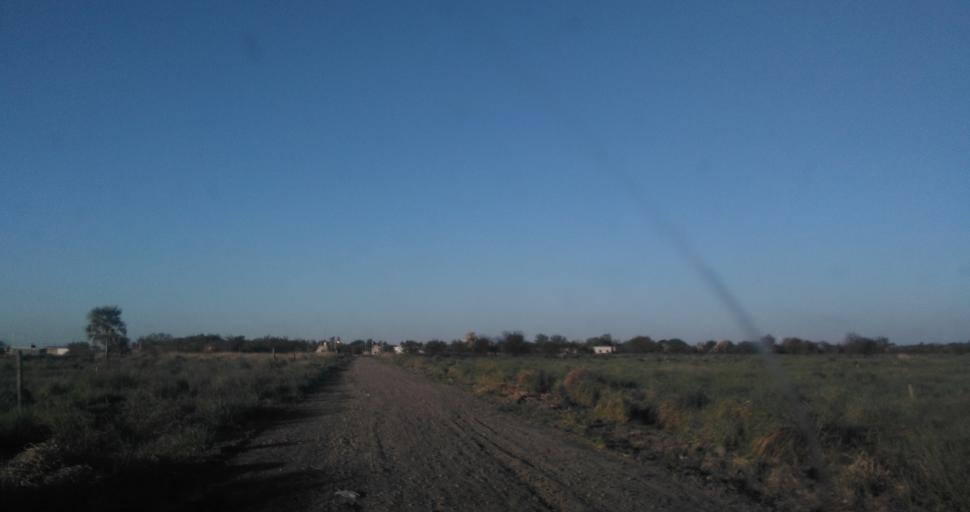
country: AR
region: Chaco
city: Resistencia
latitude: -27.4749
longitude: -59.0253
